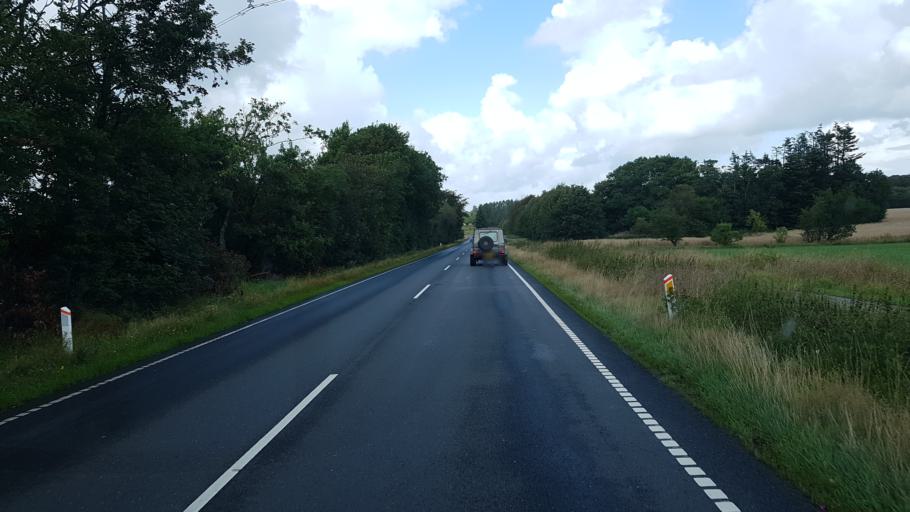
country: DK
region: South Denmark
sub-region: Vejen Kommune
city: Vejen
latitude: 55.5117
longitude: 9.1284
